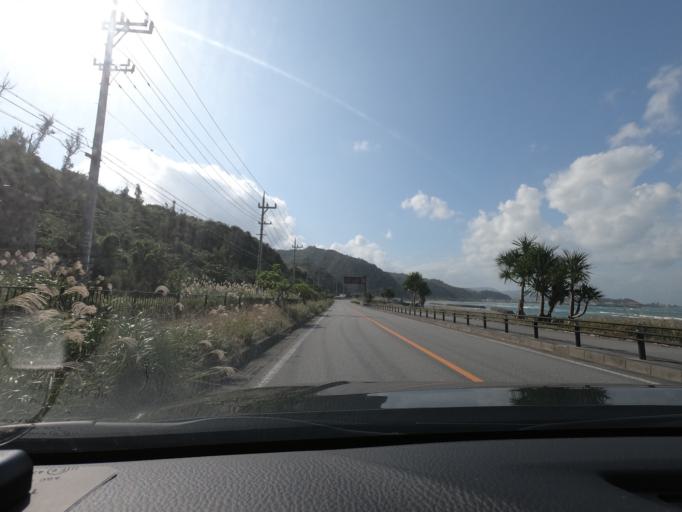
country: JP
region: Okinawa
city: Nago
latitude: 26.7591
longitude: 128.1894
